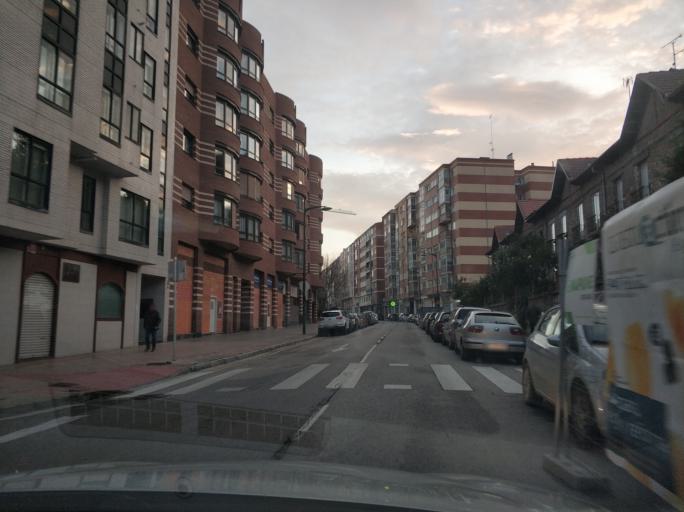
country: ES
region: Castille and Leon
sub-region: Provincia de Burgos
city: Burgos
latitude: 42.3470
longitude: -3.7008
